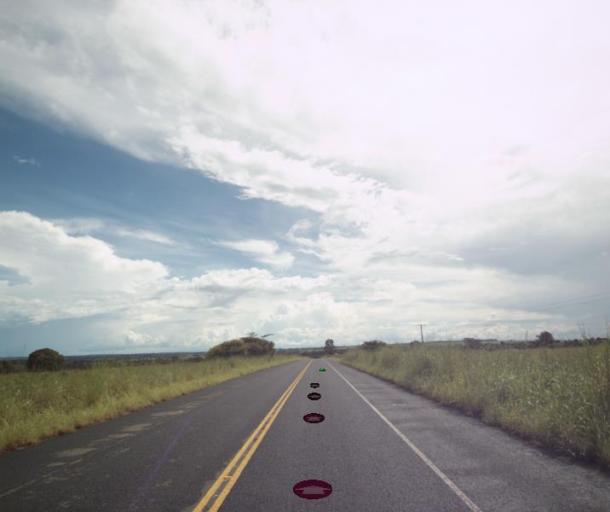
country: BR
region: Goias
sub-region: Sao Miguel Do Araguaia
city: Sao Miguel do Araguaia
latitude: -13.3014
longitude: -50.2630
